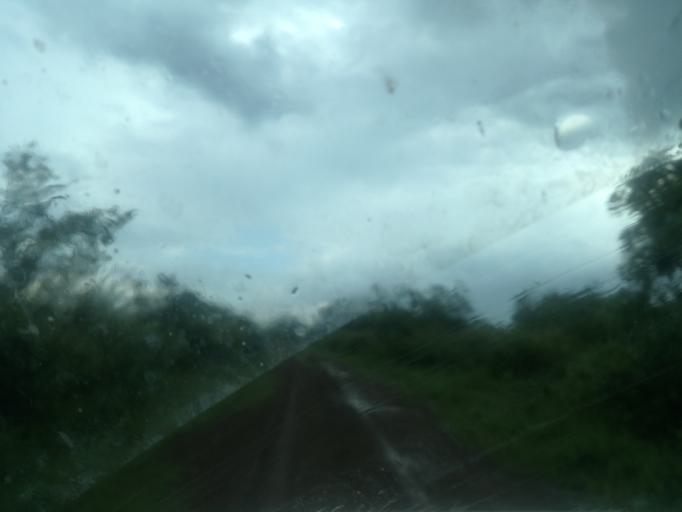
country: TZ
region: Mara
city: Issenye
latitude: -1.8963
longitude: 34.4776
